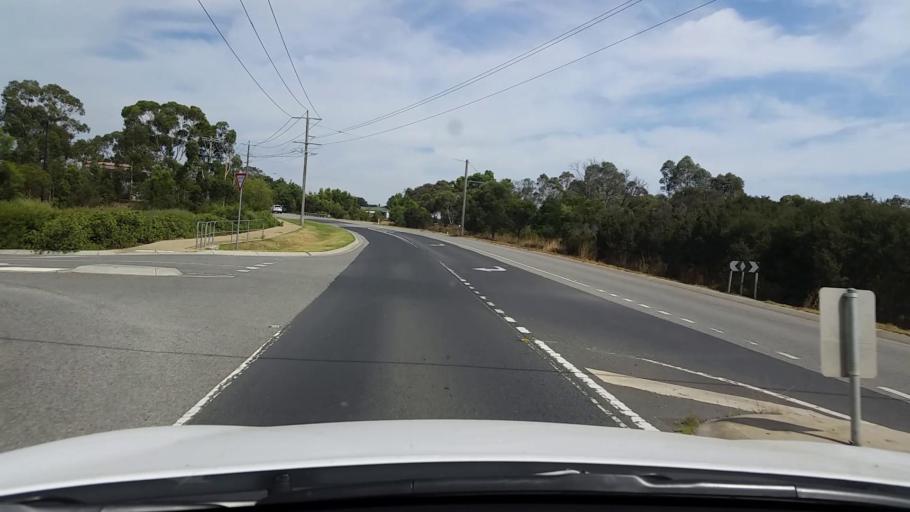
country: AU
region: Victoria
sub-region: Mornington Peninsula
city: Hastings
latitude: -38.2849
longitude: 145.1859
